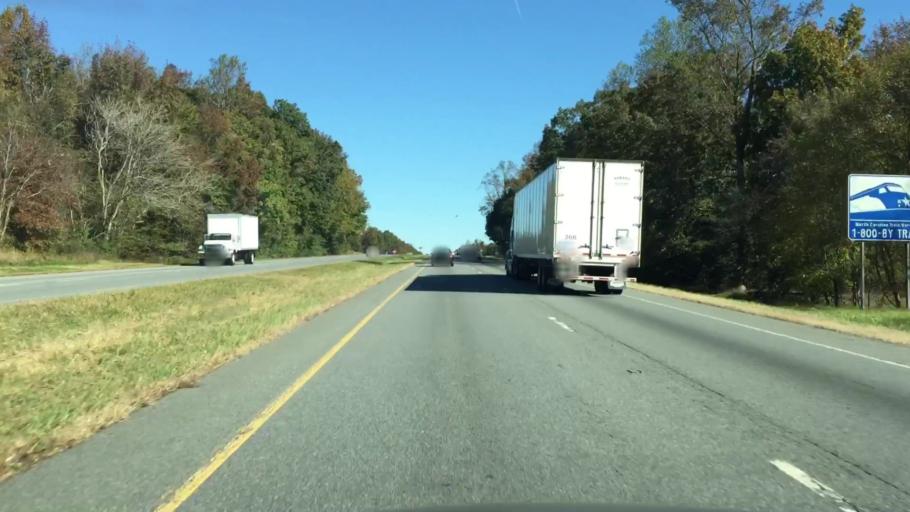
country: US
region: North Carolina
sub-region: Guilford County
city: McLeansville
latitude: 36.1949
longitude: -79.7000
